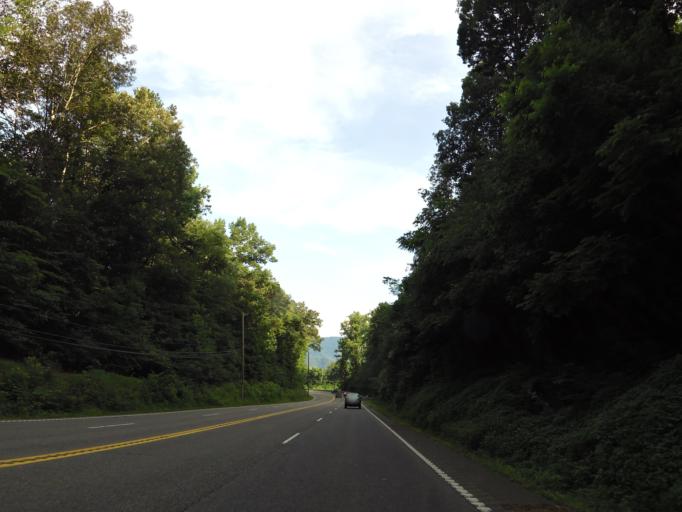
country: US
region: Tennessee
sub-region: Sevier County
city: Seymour
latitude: 35.8503
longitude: -83.7131
